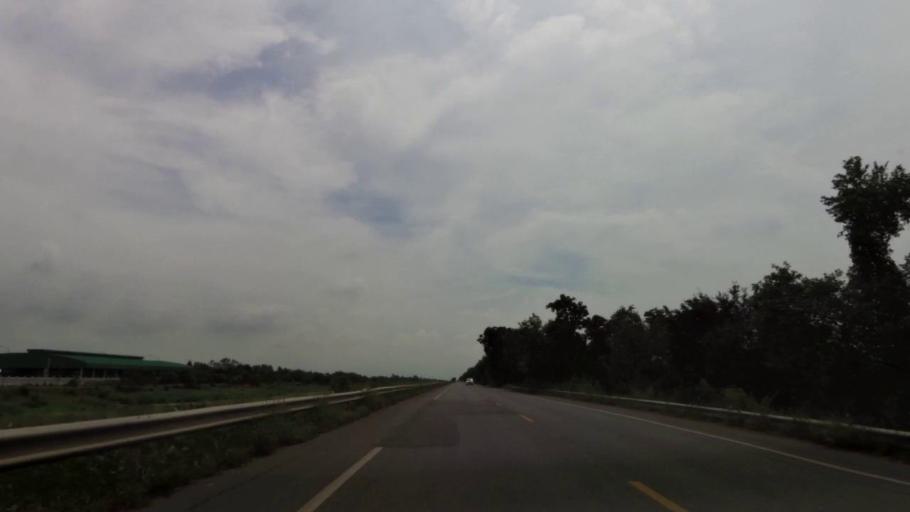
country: TH
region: Lop Buri
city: Ban Mi
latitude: 15.0424
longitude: 100.5650
